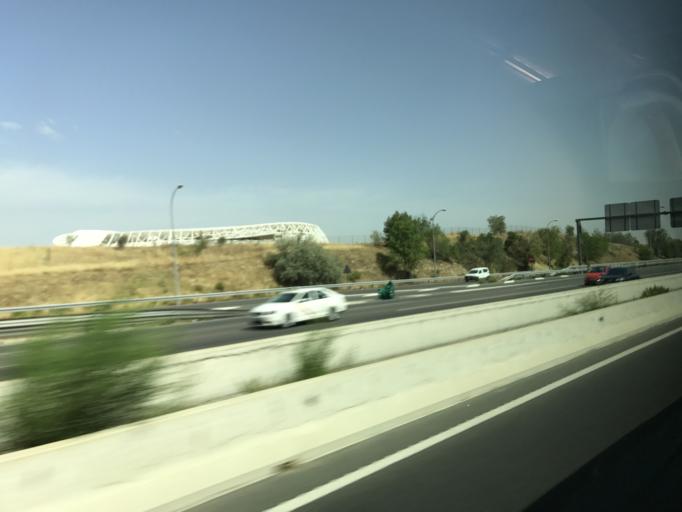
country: ES
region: Madrid
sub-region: Provincia de Madrid
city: San Blas
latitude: 40.4316
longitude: -3.5960
